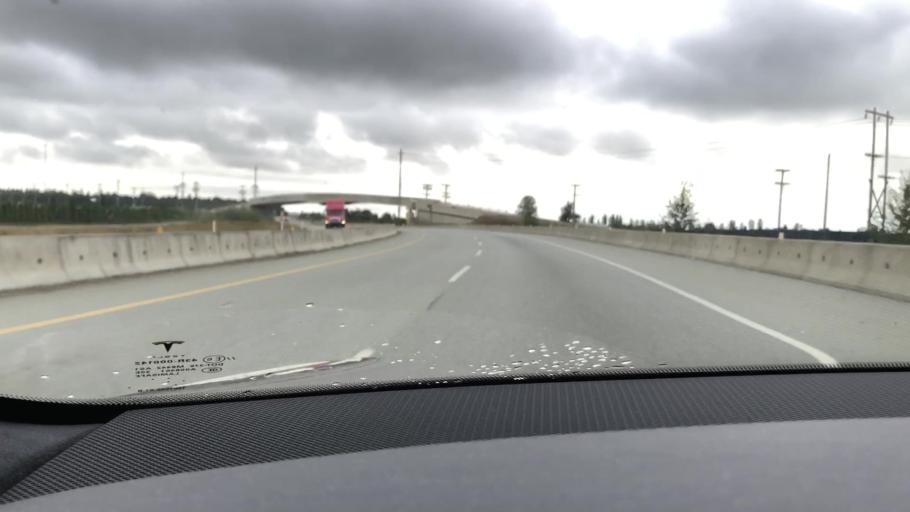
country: CA
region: British Columbia
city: Ladner
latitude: 49.1255
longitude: -123.0229
